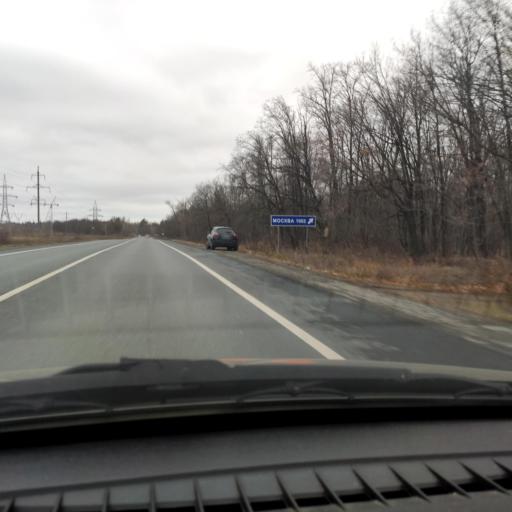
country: RU
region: Samara
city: Bogatyr'
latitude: 53.5075
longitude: 49.9360
